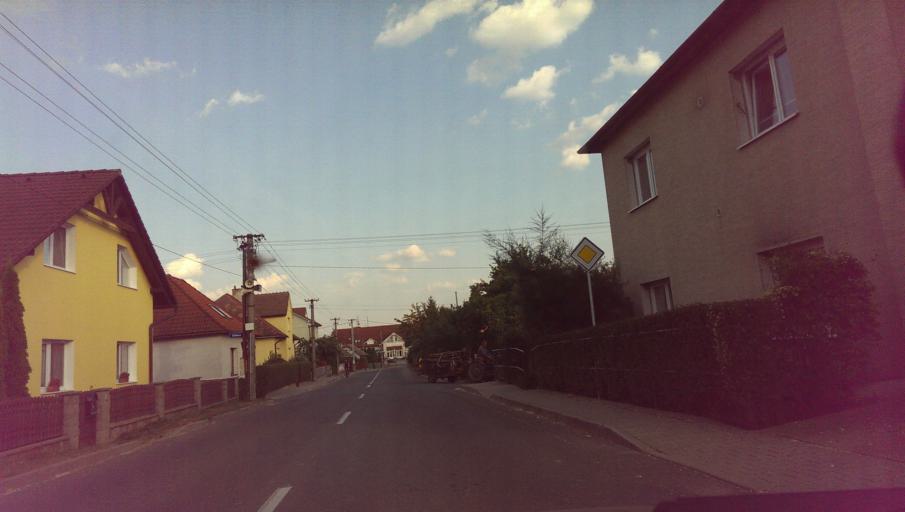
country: CZ
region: Zlin
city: Hvozdna
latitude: 49.2579
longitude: 17.7545
